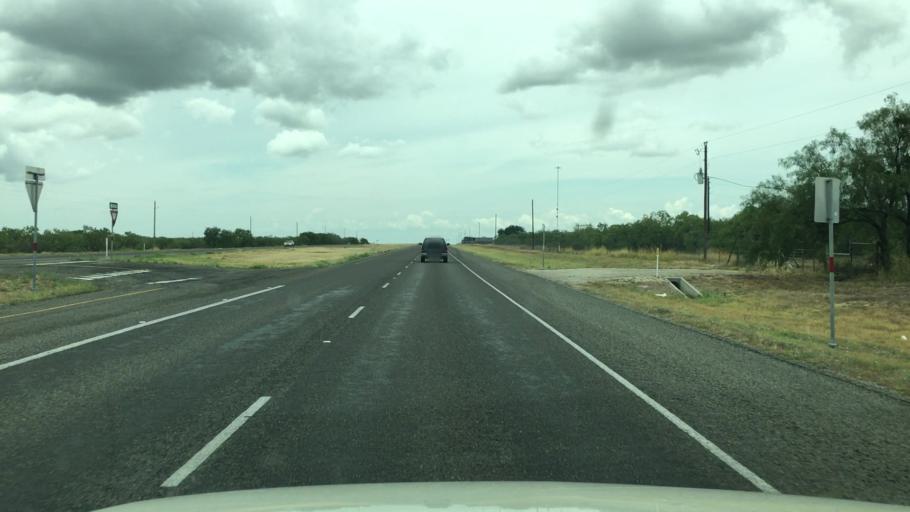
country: US
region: Texas
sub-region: Concho County
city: Eden
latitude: 31.2219
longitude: -99.9710
